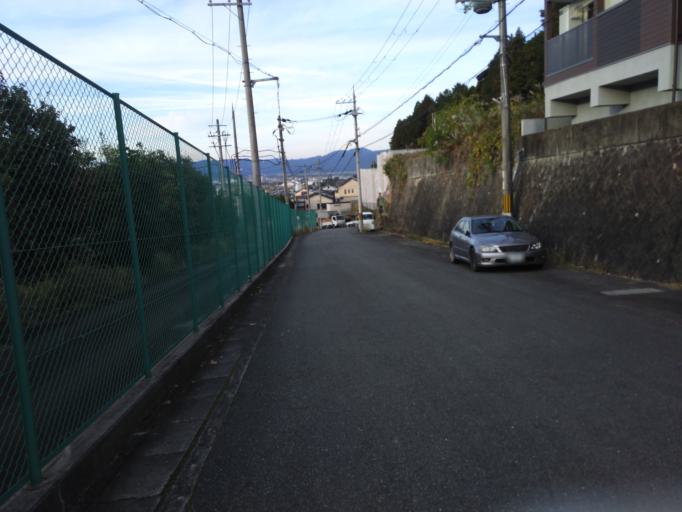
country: JP
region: Kyoto
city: Kameoka
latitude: 34.9948
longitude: 135.5557
